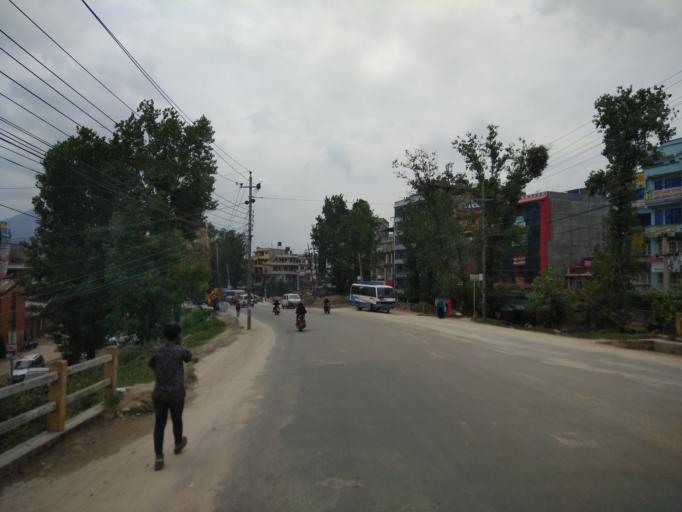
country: NP
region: Central Region
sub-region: Bagmati Zone
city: Kathmandu
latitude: 27.7417
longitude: 85.3336
